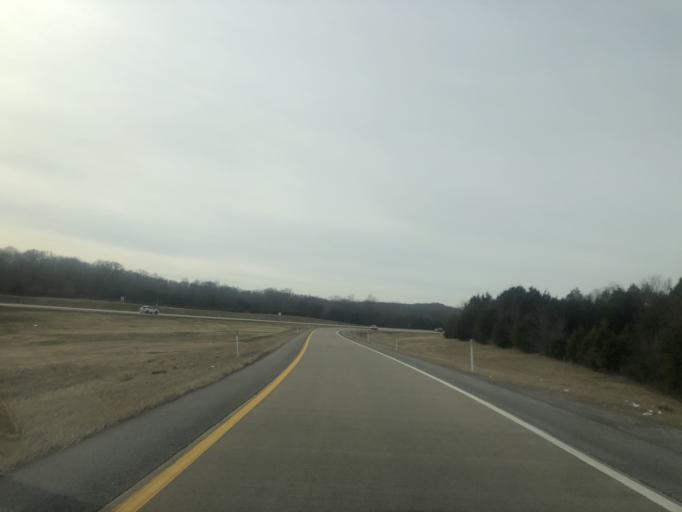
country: US
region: Tennessee
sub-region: Williamson County
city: Nolensville
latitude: 35.8598
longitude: -86.5813
